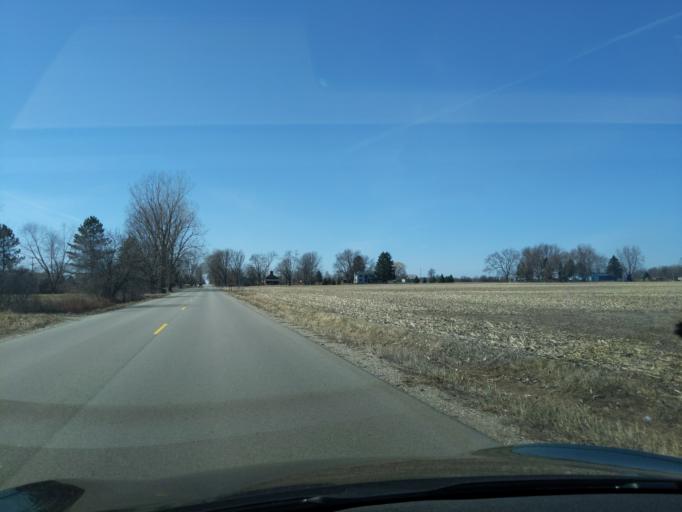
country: US
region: Michigan
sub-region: Eaton County
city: Grand Ledge
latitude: 42.7265
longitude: -84.8144
